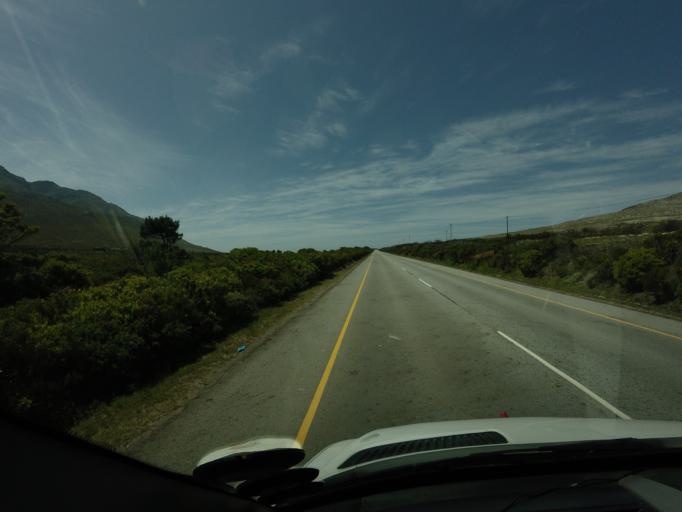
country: ZA
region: Western Cape
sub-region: Overberg District Municipality
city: Grabouw
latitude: -34.3449
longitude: 18.8493
